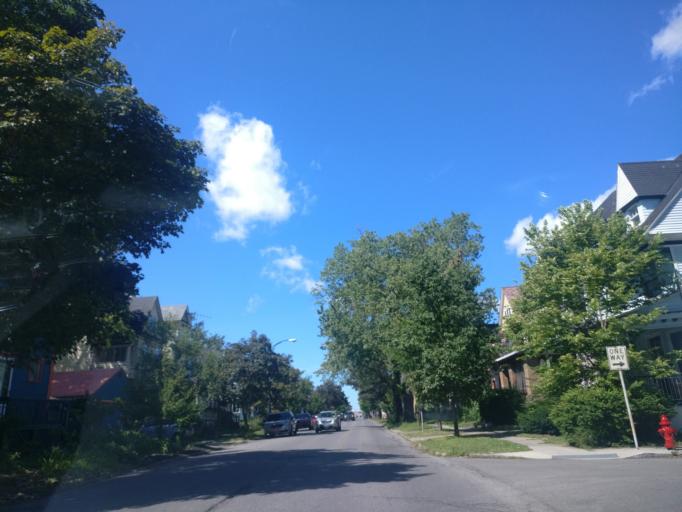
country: US
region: New York
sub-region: Erie County
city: Buffalo
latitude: 42.9155
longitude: -78.8832
